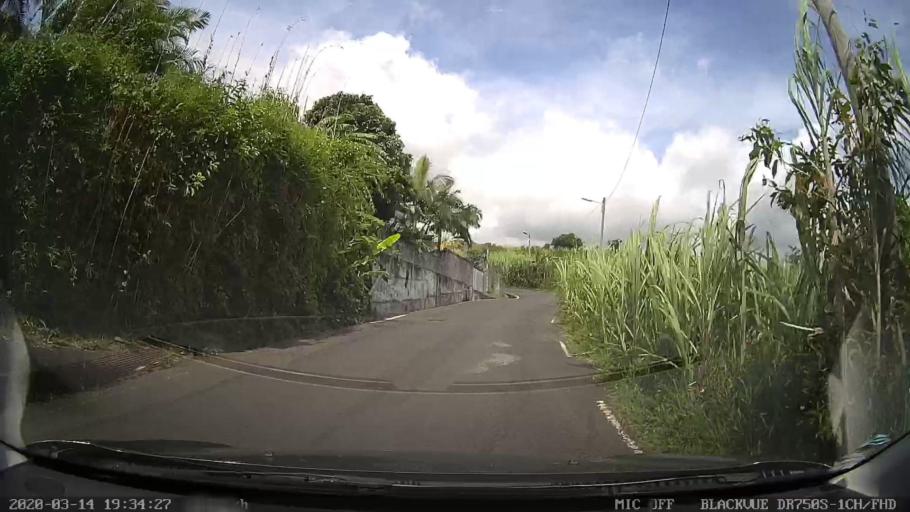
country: RE
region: Reunion
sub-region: Reunion
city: Sainte-Marie
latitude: -20.9341
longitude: 55.5251
